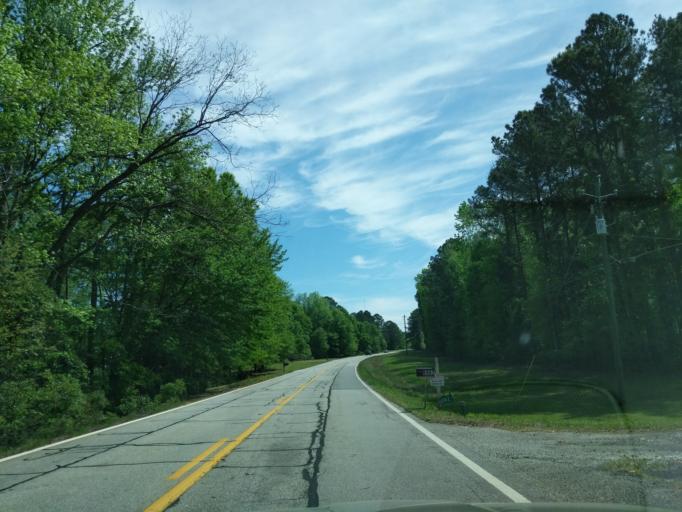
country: US
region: Georgia
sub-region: Columbia County
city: Appling
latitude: 33.6120
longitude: -82.3137
